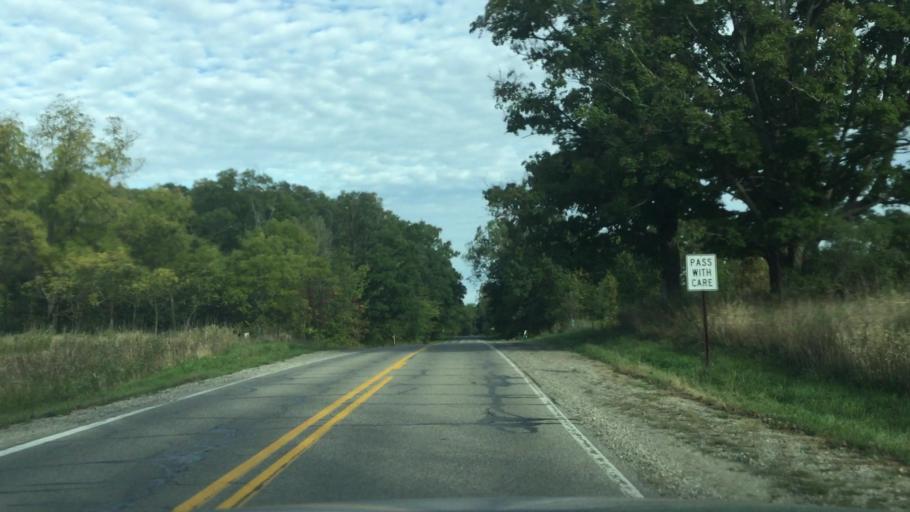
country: US
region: Michigan
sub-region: Livingston County
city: Howell
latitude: 42.5439
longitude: -83.8766
